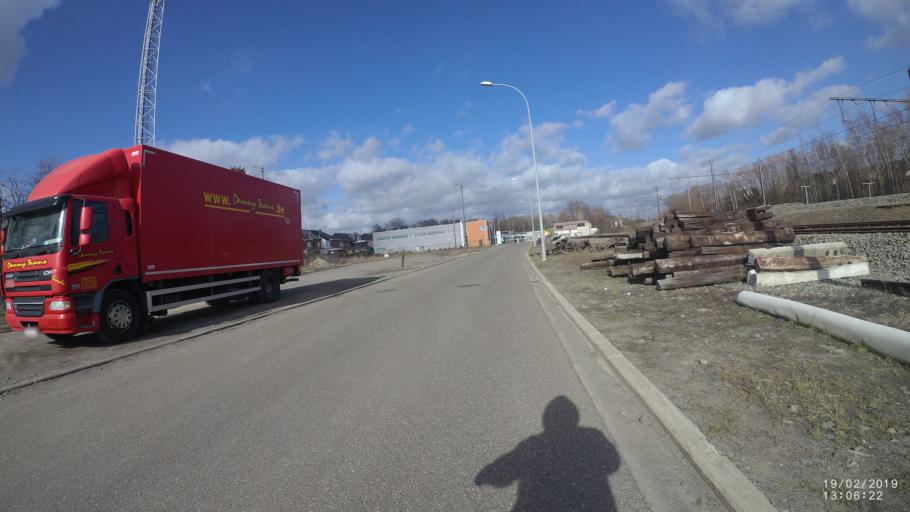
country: BE
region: Flanders
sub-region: Provincie Limburg
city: Tongeren
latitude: 50.7861
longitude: 5.4730
